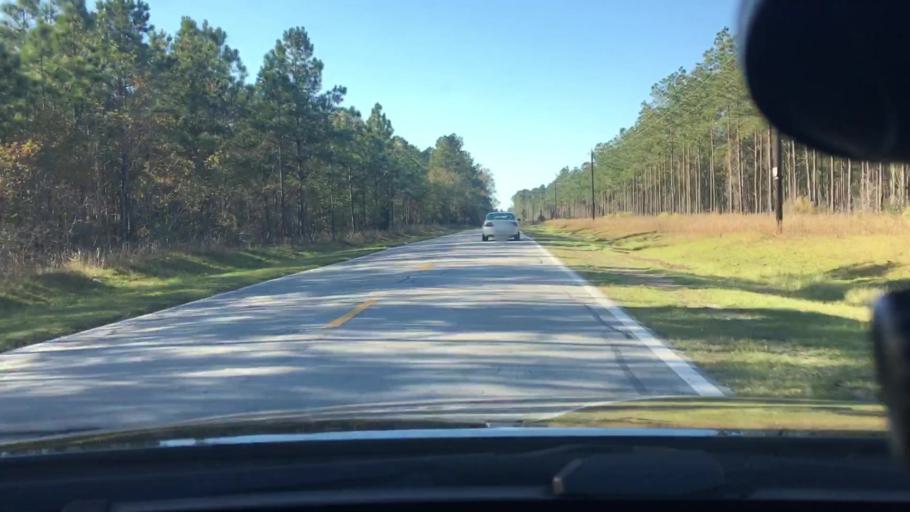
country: US
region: North Carolina
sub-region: Craven County
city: Vanceboro
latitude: 35.2234
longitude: -77.1284
